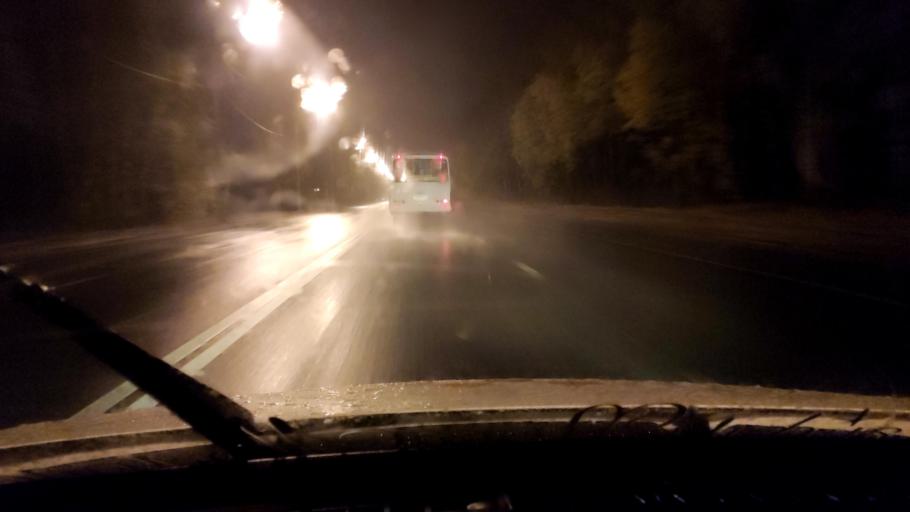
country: RU
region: Voronezj
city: Pridonskoy
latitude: 51.6926
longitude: 39.0956
